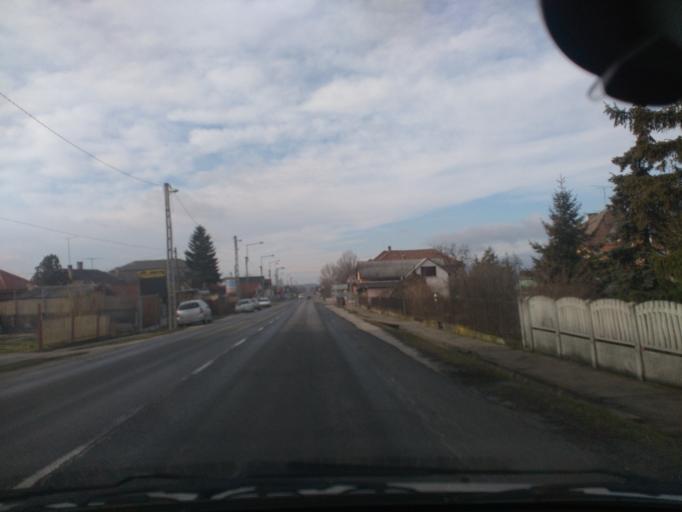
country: HU
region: Komarom-Esztergom
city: Tokod
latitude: 47.7322
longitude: 18.6904
